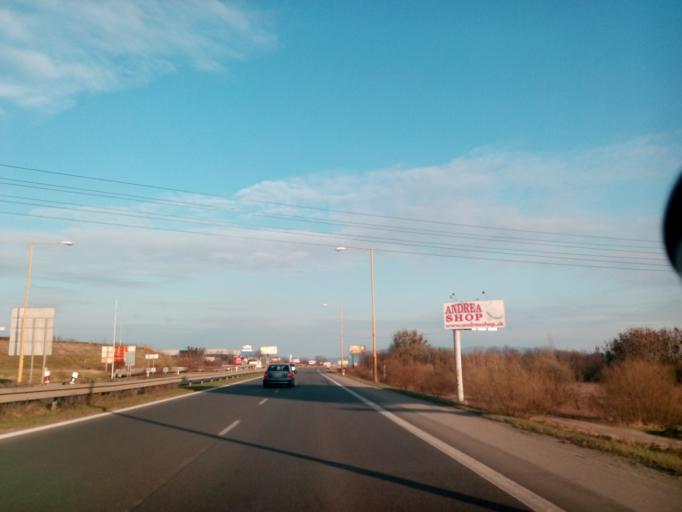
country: SK
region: Kosicky
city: Kosice
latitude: 48.6928
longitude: 21.2374
